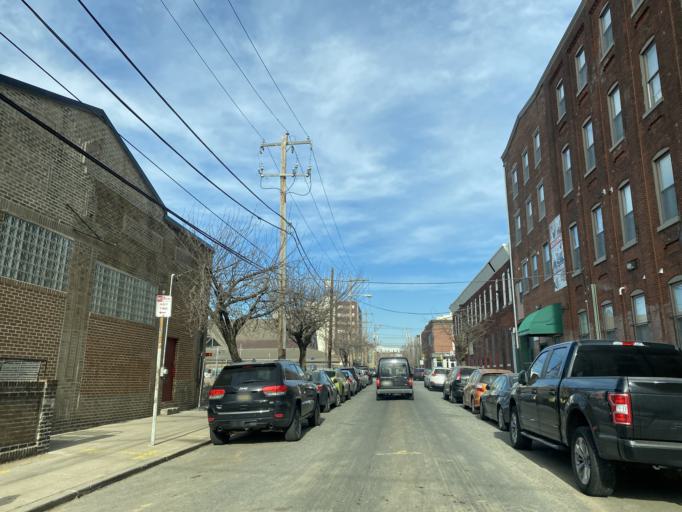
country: US
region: Pennsylvania
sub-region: Philadelphia County
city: Philadelphia
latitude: 39.9690
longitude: -75.1417
